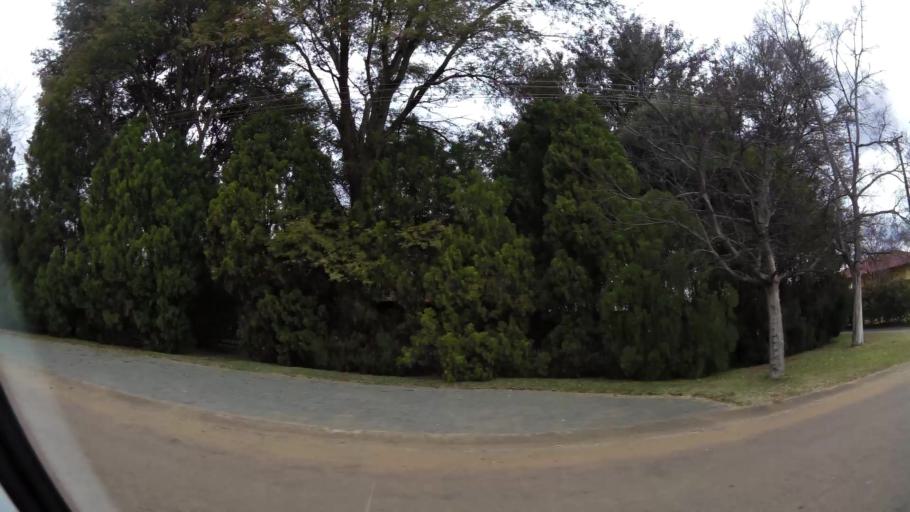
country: ZA
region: Limpopo
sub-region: Waterberg District Municipality
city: Modimolle
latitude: -24.7058
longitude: 28.4154
